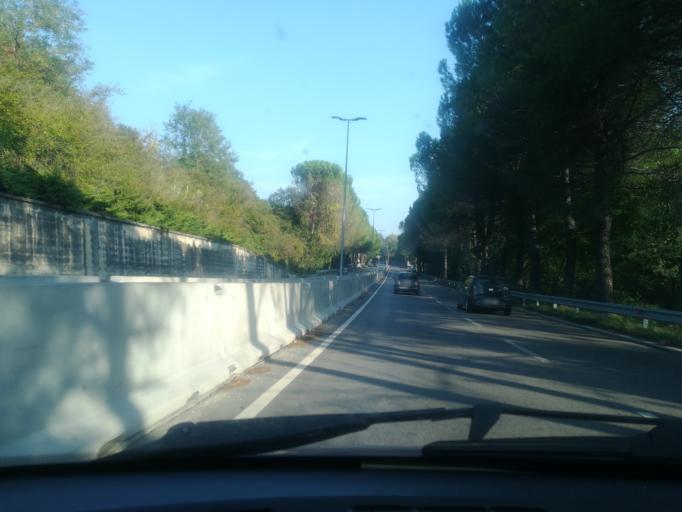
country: IT
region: The Marches
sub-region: Provincia di Macerata
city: Macerata
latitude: 43.2910
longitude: 13.4443
